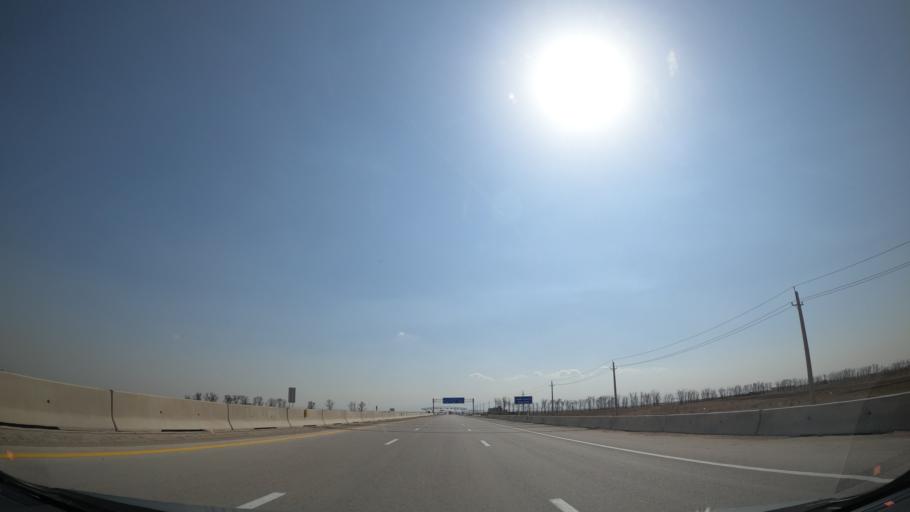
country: IR
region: Qazvin
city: Abyek
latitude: 35.9643
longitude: 50.4627
